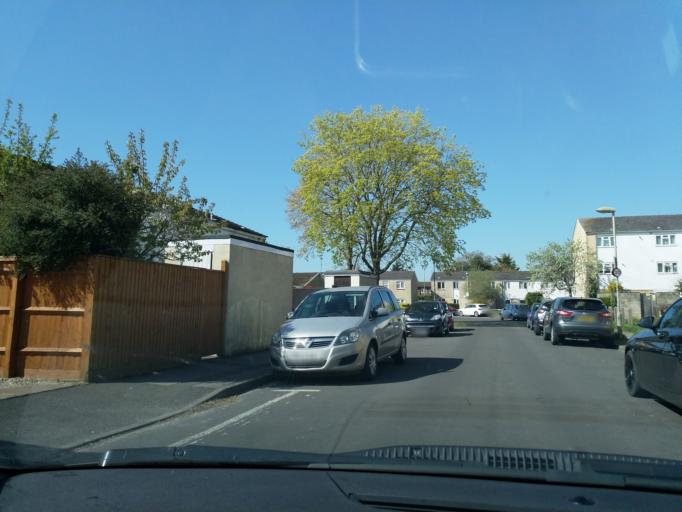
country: GB
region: England
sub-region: Oxfordshire
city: Cowley
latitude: 51.7489
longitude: -1.2026
